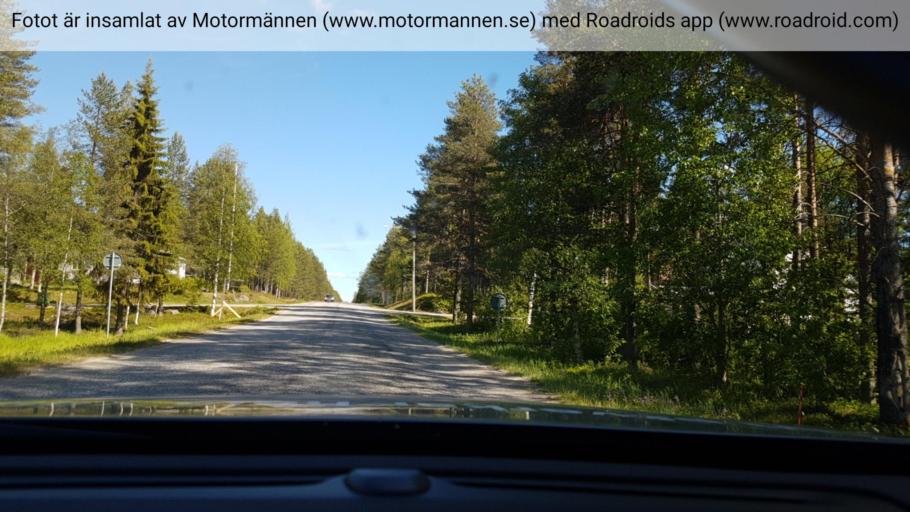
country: SE
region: Vaesterbotten
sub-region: Lycksele Kommun
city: Soderfors
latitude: 64.6259
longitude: 18.0725
